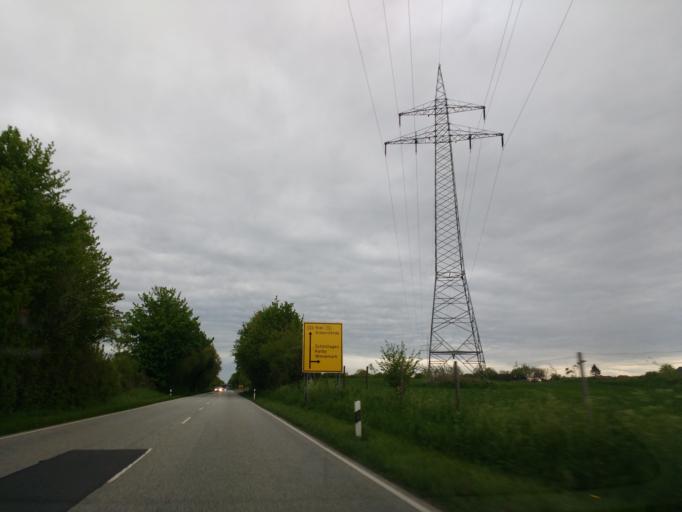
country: DE
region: Schleswig-Holstein
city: Dorphof
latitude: 54.6339
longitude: 9.9632
